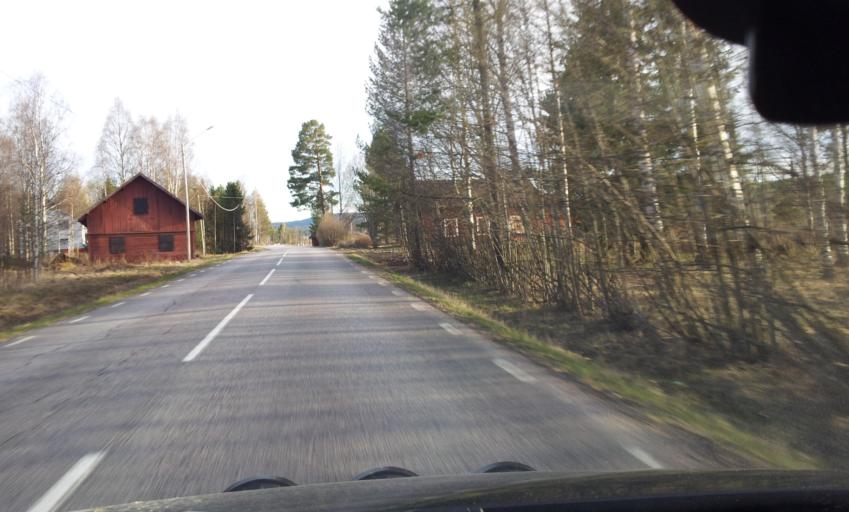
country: SE
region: Vaesternorrland
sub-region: Ange Kommun
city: Ange
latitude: 62.1648
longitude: 15.6791
